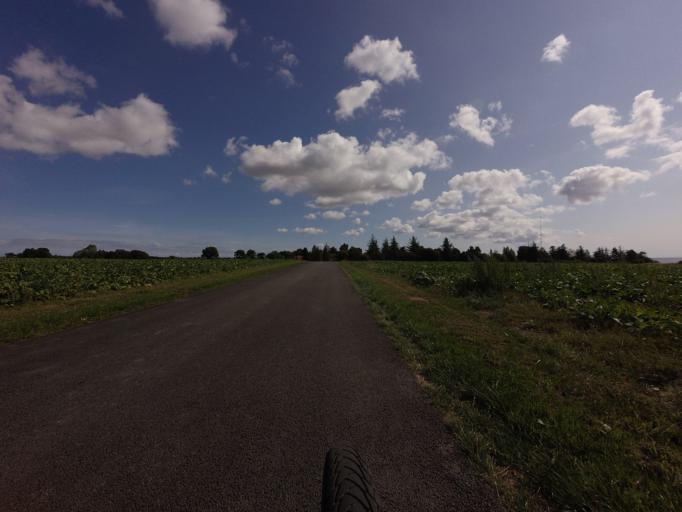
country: DK
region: Zealand
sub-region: Vordingborg Kommune
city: Stege
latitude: 54.9656
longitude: 12.3503
